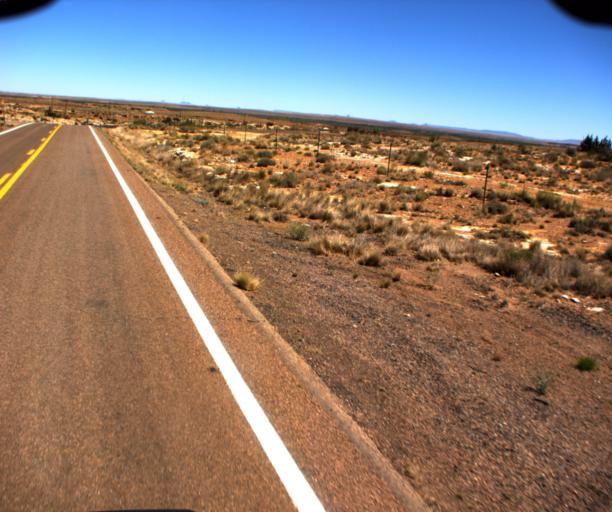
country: US
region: Arizona
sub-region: Navajo County
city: Winslow
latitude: 34.9653
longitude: -110.6468
